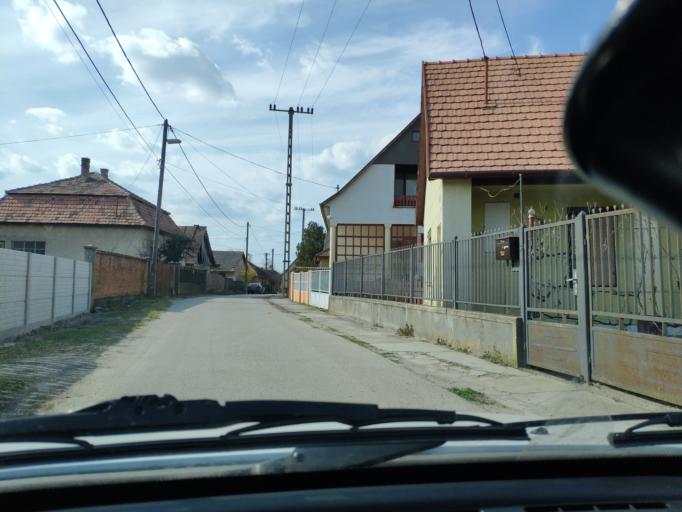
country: HU
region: Pest
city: Rackeve
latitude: 47.1644
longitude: 18.9408
